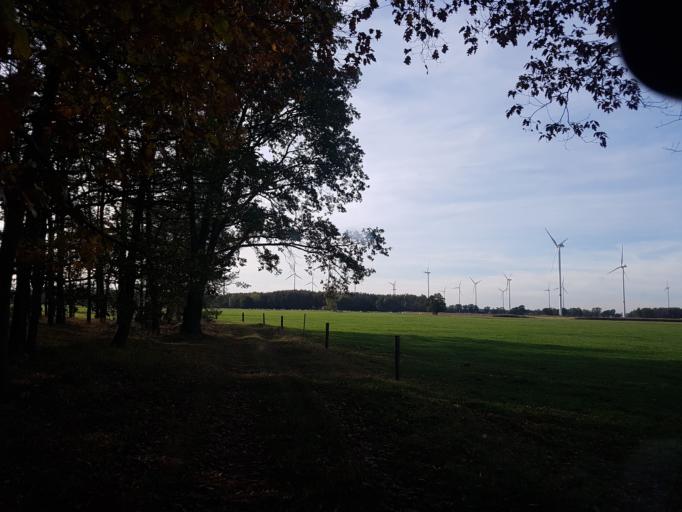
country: DE
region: Brandenburg
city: Schilda
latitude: 51.5666
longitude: 13.3223
